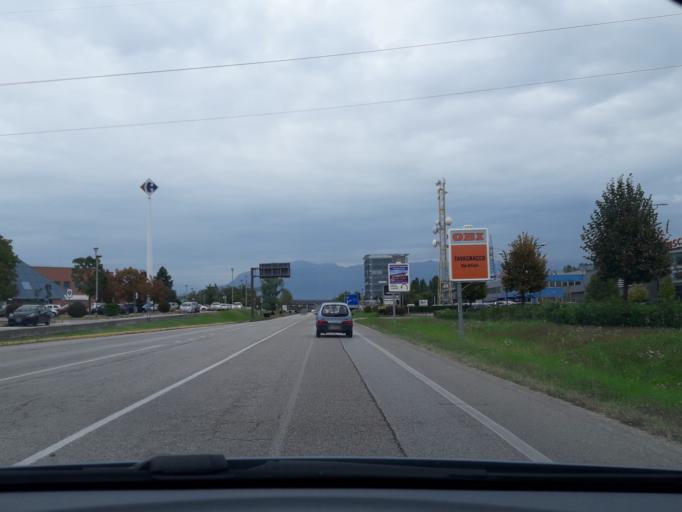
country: IT
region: Friuli Venezia Giulia
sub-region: Provincia di Udine
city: Tavagnacco
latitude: 46.1183
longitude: 13.2264
